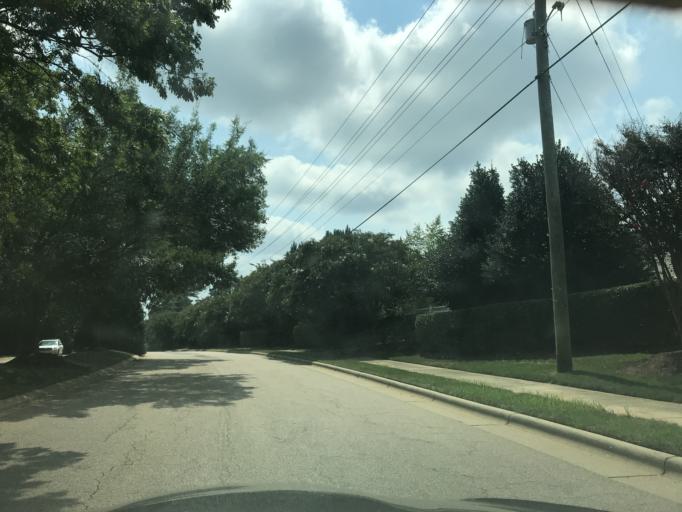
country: US
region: North Carolina
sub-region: Wake County
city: Wake Forest
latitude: 35.9254
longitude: -78.5840
